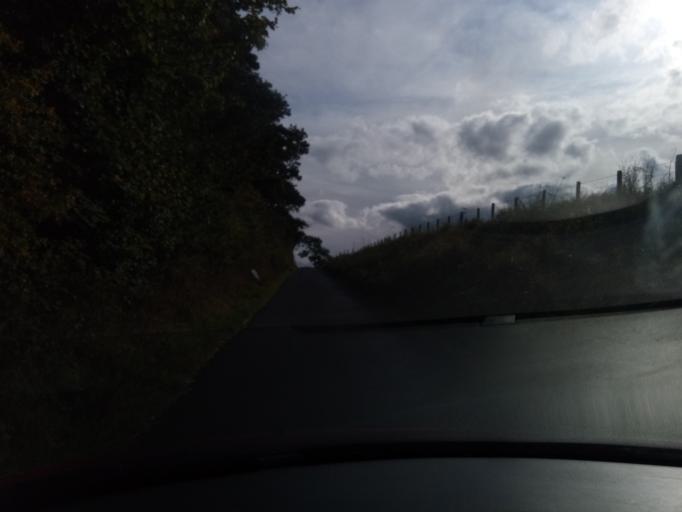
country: GB
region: Scotland
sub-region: The Scottish Borders
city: Kelso
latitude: 55.4764
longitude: -2.3530
